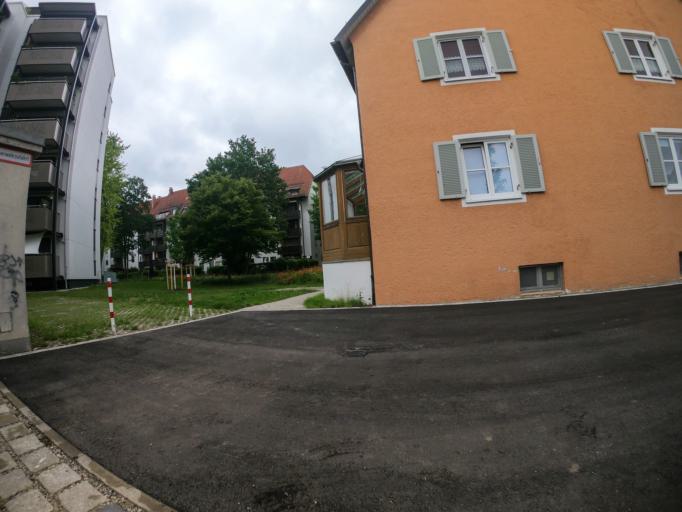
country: DE
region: Bavaria
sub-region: Lower Bavaria
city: Landshut
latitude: 48.5454
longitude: 12.1576
